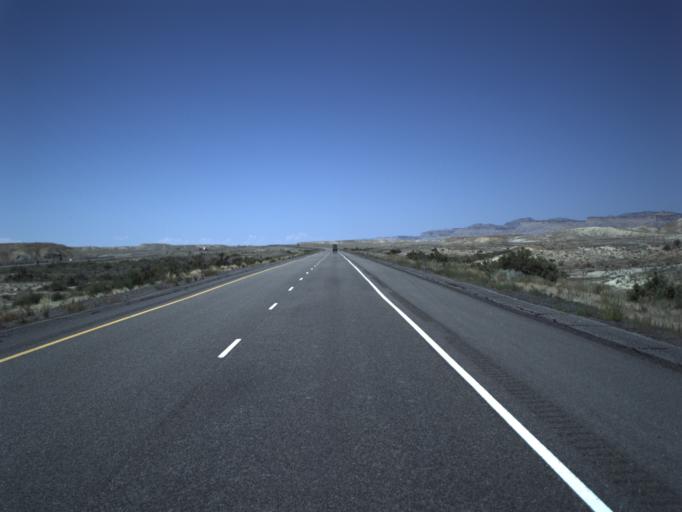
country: US
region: Utah
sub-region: Grand County
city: Moab
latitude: 38.9411
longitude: -109.5135
